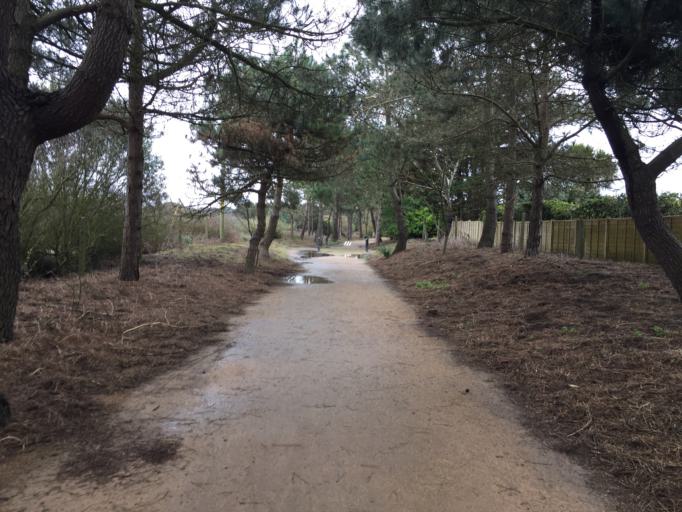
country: JE
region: St Helier
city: Saint Helier
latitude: 49.1821
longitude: -2.2350
